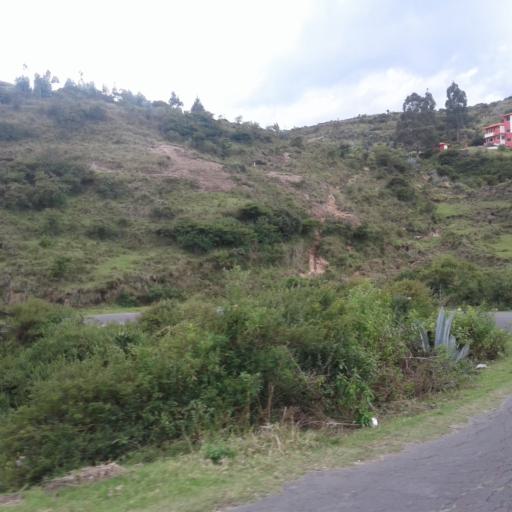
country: EC
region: Pichincha
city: Sangolqui
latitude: -0.2889
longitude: -78.3883
